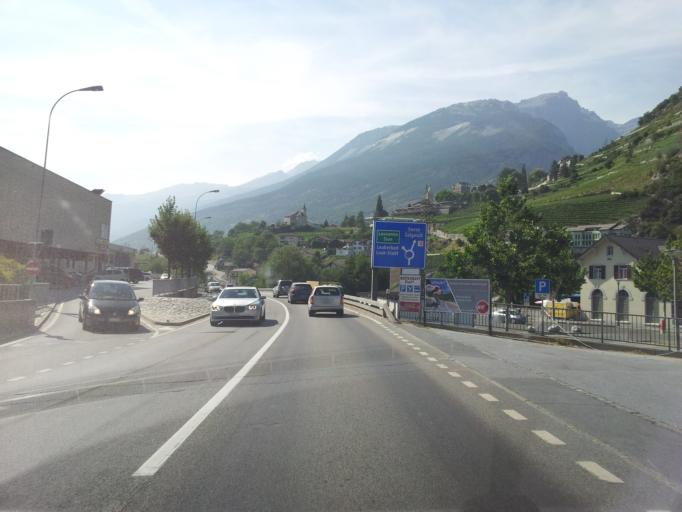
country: CH
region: Valais
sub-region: Leuk District
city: Leuk
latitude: 46.3115
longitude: 7.6422
